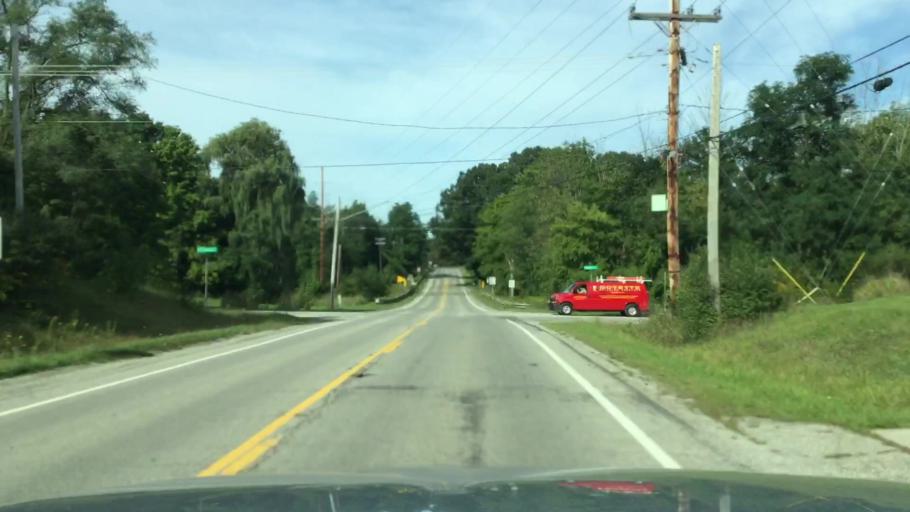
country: US
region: Michigan
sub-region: Genesee County
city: Montrose
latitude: 43.1180
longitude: -83.8920
